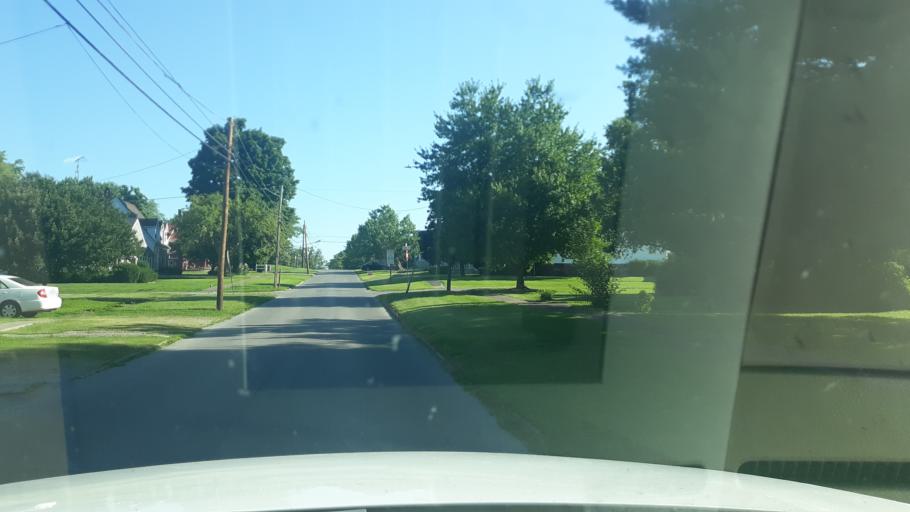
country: US
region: Illinois
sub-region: Saline County
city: Eldorado
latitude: 37.8183
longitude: -88.4361
